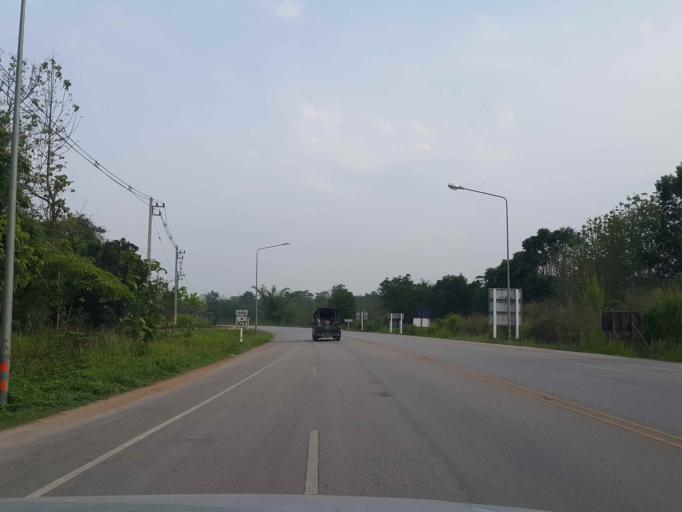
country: TH
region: Chiang Mai
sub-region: Amphoe Chiang Dao
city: Chiang Dao
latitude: 19.3764
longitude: 98.9462
